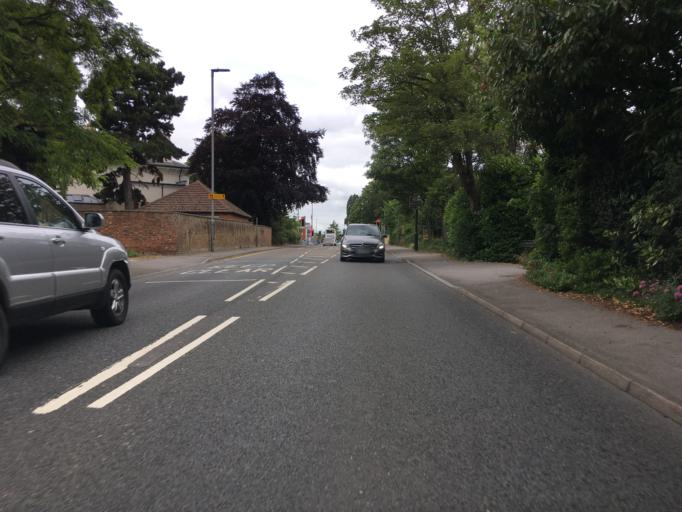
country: GB
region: England
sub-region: Gloucestershire
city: Charlton Kings
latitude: 51.8874
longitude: -2.0513
